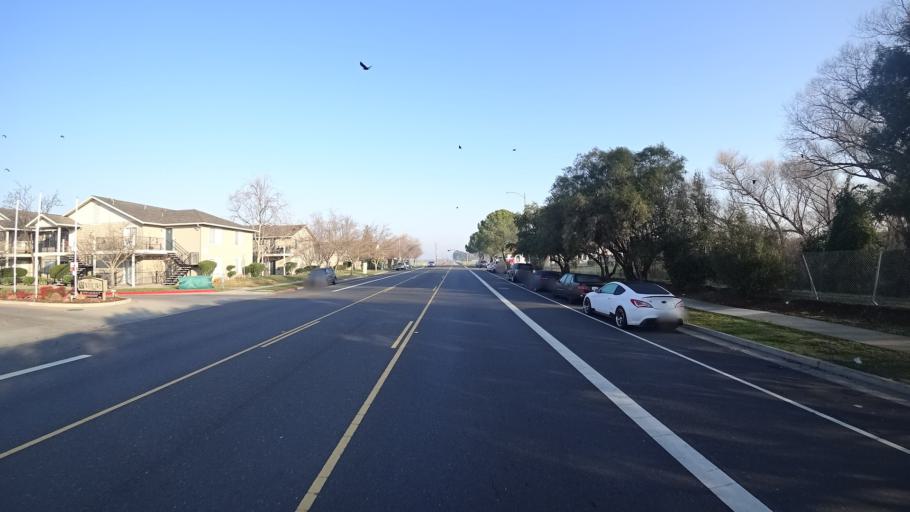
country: US
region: California
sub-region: Yolo County
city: Davis
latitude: 38.5596
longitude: -121.7862
